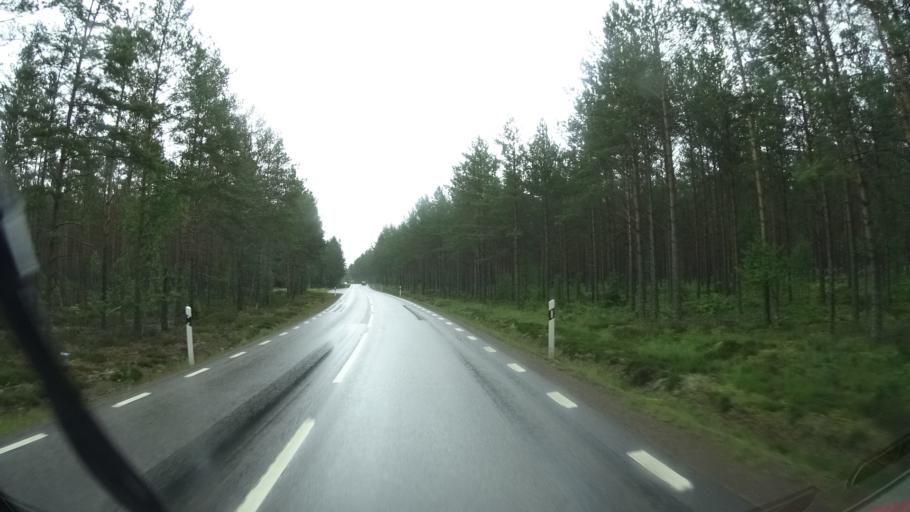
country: SE
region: Kalmar
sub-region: Hultsfreds Kommun
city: Hultsfred
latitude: 57.5161
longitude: 15.8134
